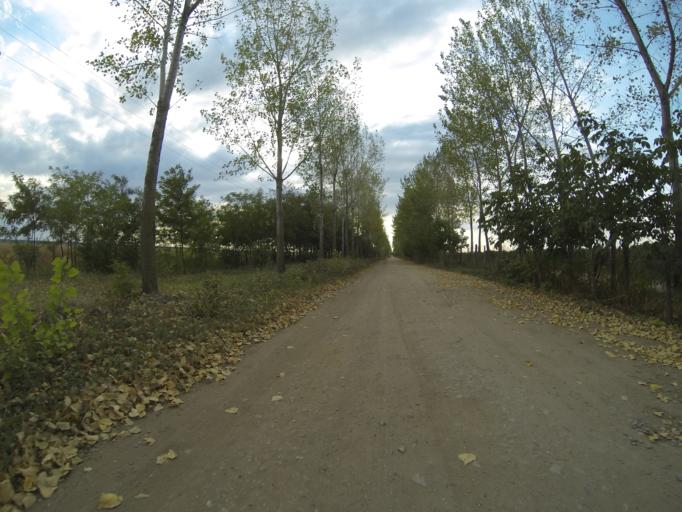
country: RO
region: Dolj
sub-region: Comuna Segarcea
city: Segarcea
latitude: 44.1032
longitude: 23.7113
